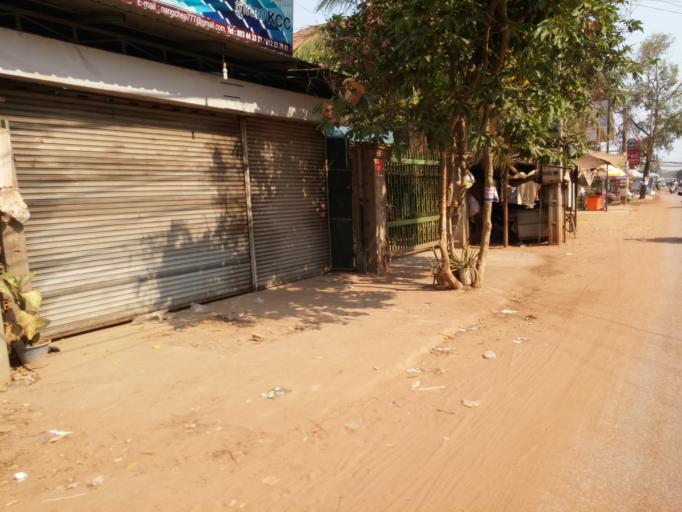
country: KH
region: Siem Reap
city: Siem Reap
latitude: 13.3778
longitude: 103.8515
